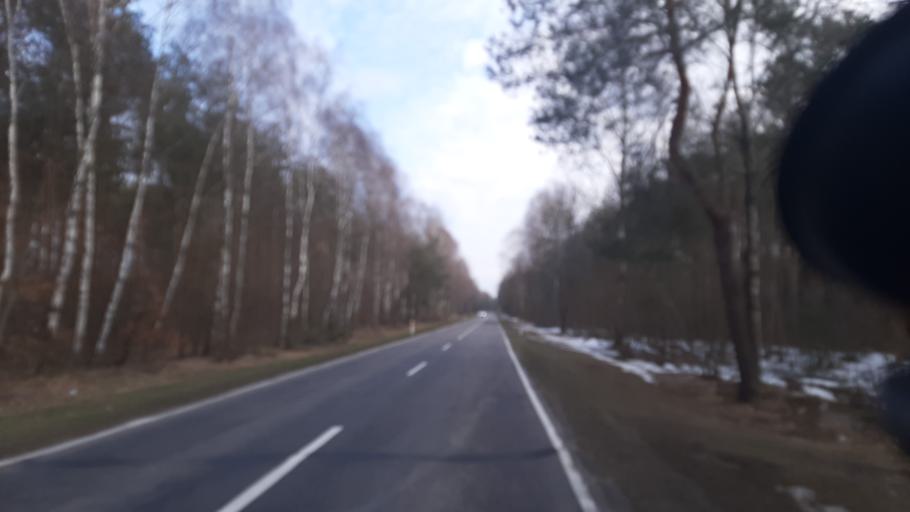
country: PL
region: Lublin Voivodeship
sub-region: Powiat lubartowski
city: Ostrow Lubelski
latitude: 51.4911
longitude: 22.8134
